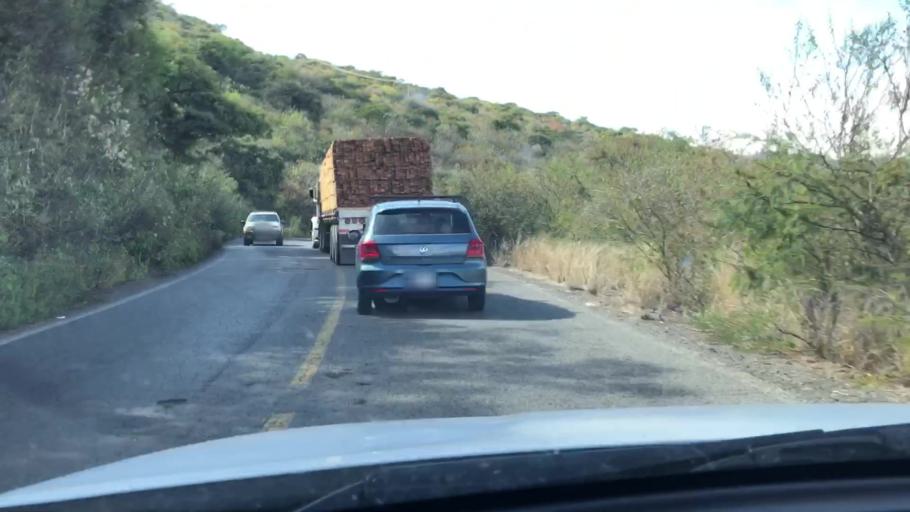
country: MX
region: Jalisco
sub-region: Zacoalco de Torres
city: Barranca de Otates (Barranca de Otatan)
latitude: 20.2294
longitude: -103.6812
